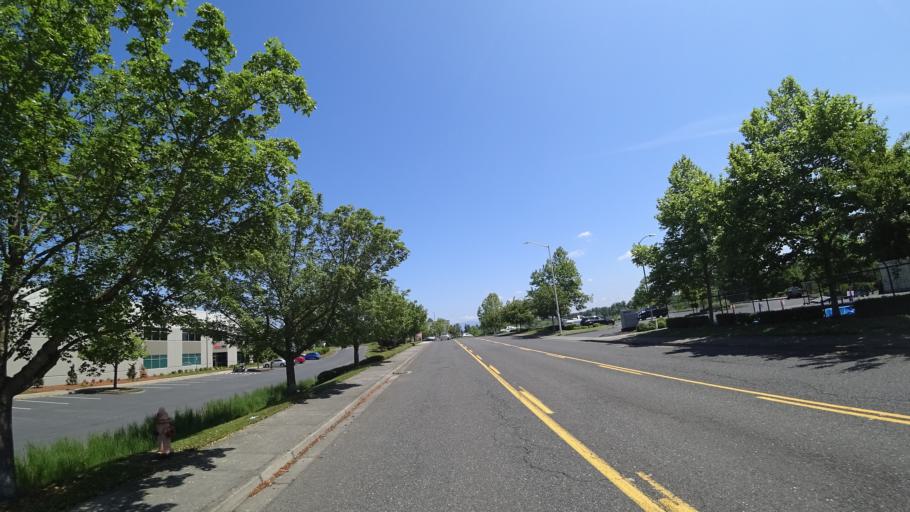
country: US
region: Oregon
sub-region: Multnomah County
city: Fairview
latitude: 45.5528
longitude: -122.4920
